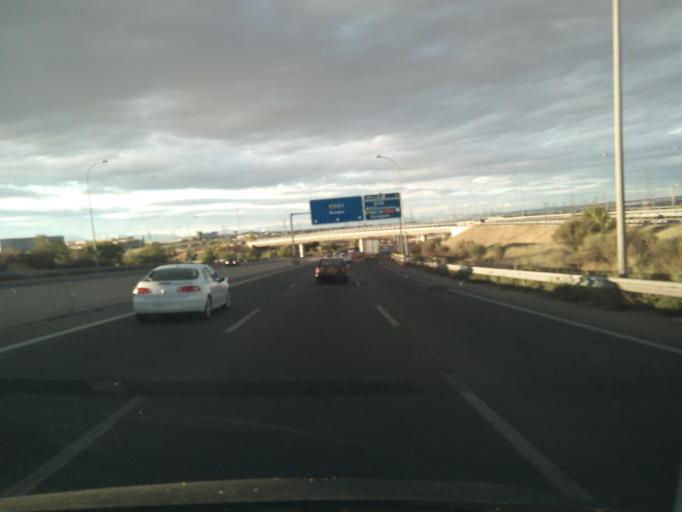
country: ES
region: Madrid
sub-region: Provincia de Madrid
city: San Sebastian de los Reyes
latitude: 40.5510
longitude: -3.6078
